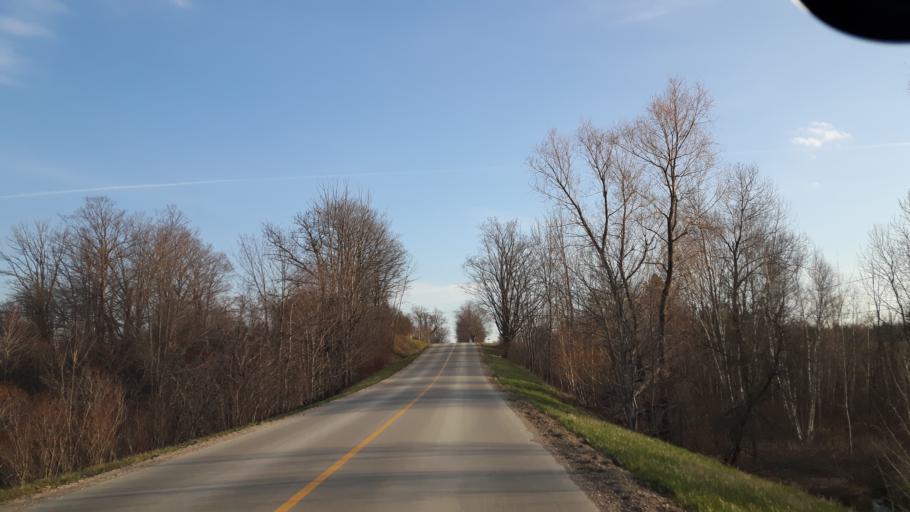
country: CA
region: Ontario
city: Goderich
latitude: 43.6446
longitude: -81.6642
